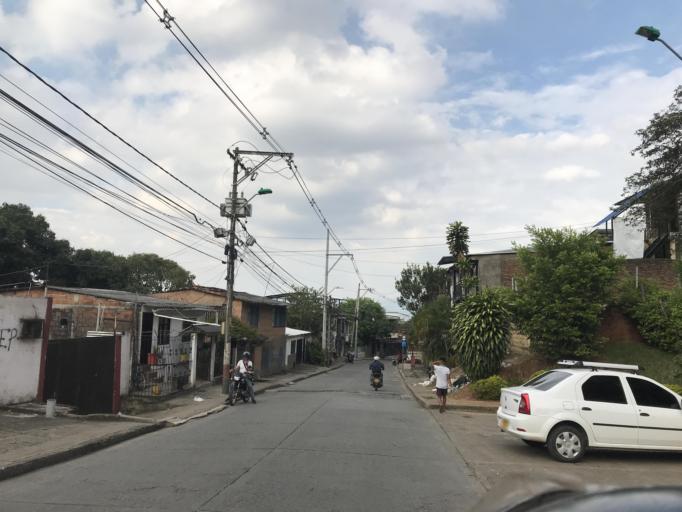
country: CO
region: Valle del Cauca
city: Cali
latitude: 3.3751
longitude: -76.5523
